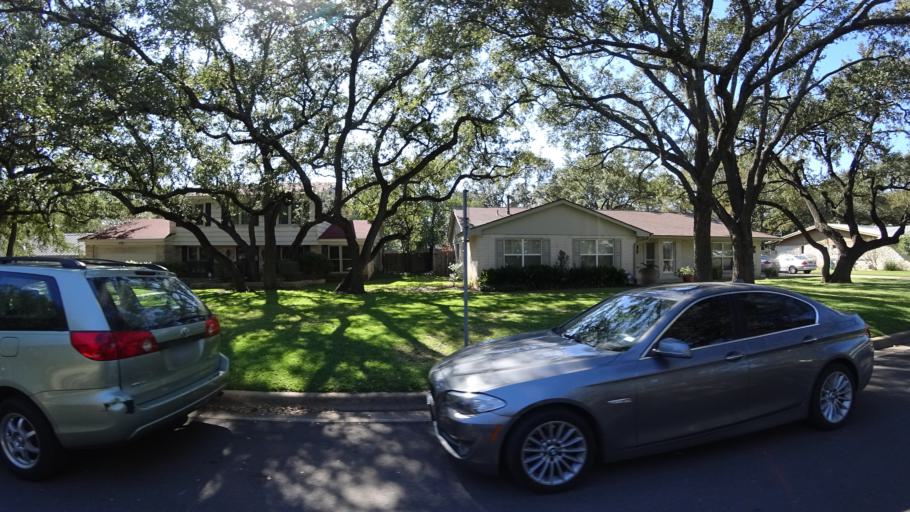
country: US
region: Texas
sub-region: Williamson County
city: Jollyville
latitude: 30.3797
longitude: -97.7502
